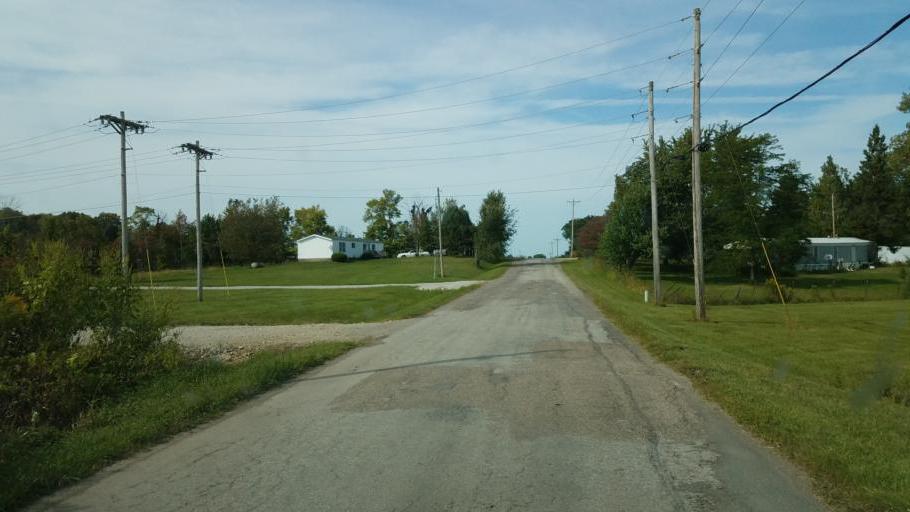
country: US
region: Ohio
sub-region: Knox County
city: Centerburg
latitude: 40.4108
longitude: -82.6513
